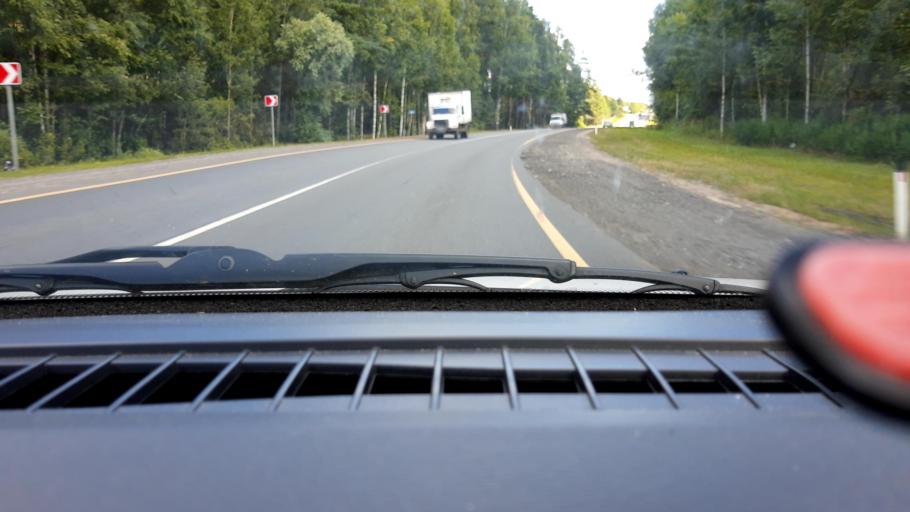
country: RU
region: Nizjnij Novgorod
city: Arzamas
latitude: 55.5104
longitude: 43.8977
